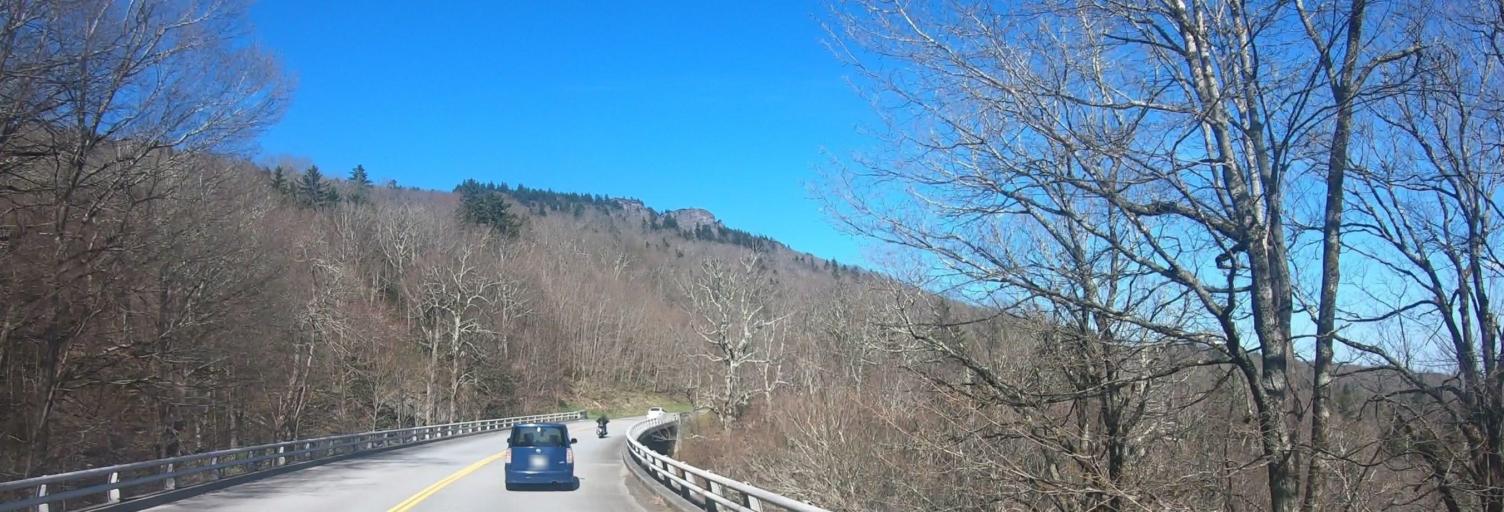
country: US
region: North Carolina
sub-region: Watauga County
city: Foscoe
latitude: 36.0989
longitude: -81.7915
